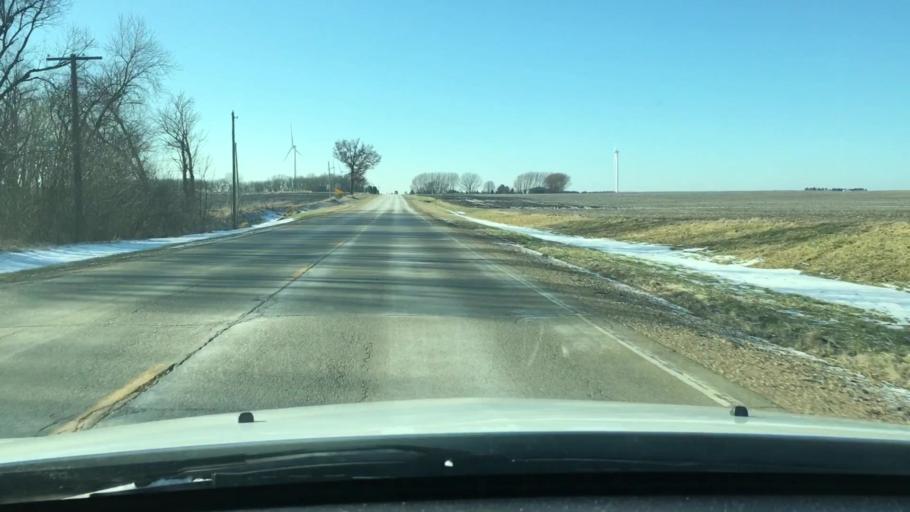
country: US
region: Illinois
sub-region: LaSalle County
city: Mendota
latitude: 41.6854
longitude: -89.1009
